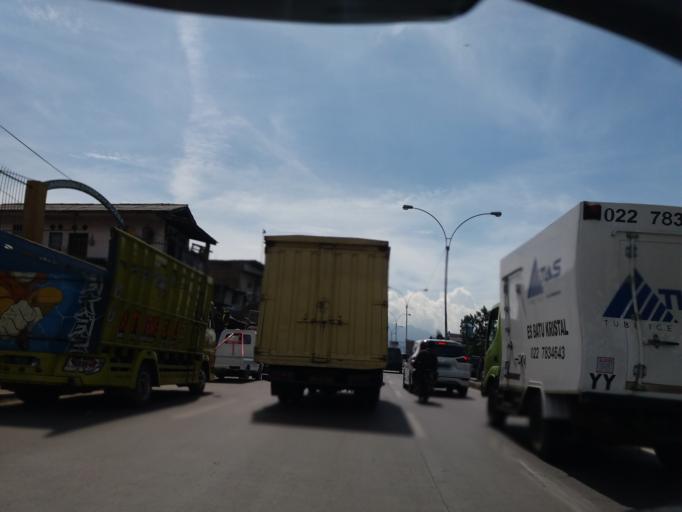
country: ID
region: West Java
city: Margahayukencana
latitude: -6.9261
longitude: 107.5753
